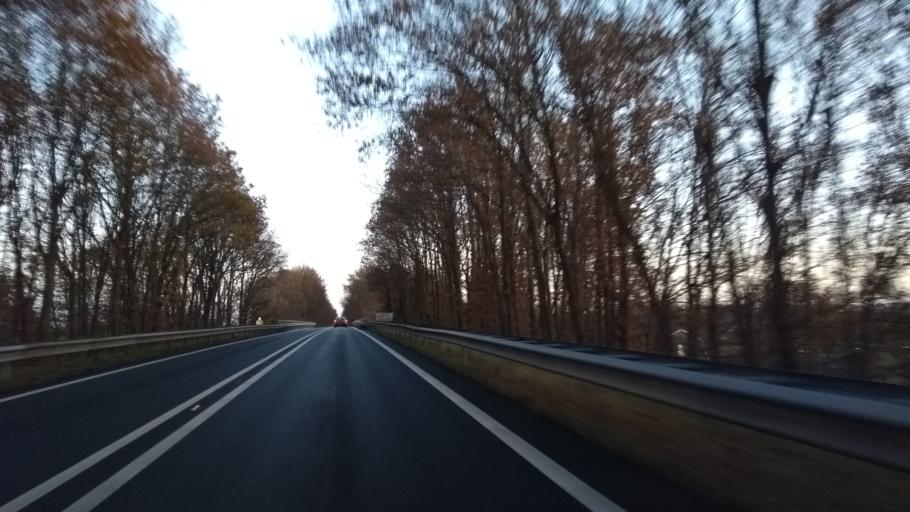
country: NL
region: Overijssel
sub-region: Gemeente Twenterand
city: Vroomshoop
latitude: 52.4987
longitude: 6.5799
